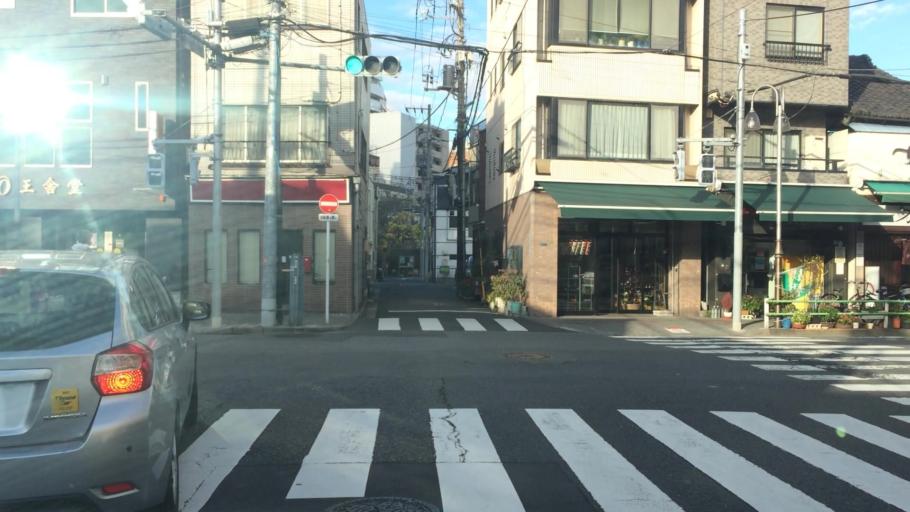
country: JP
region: Tokyo
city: Tokyo
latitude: 35.7211
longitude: 139.7861
